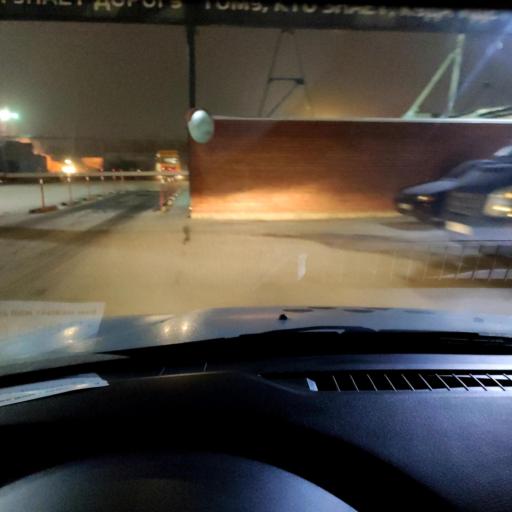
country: RU
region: Samara
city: Zhigulevsk
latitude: 53.5230
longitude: 49.4801
